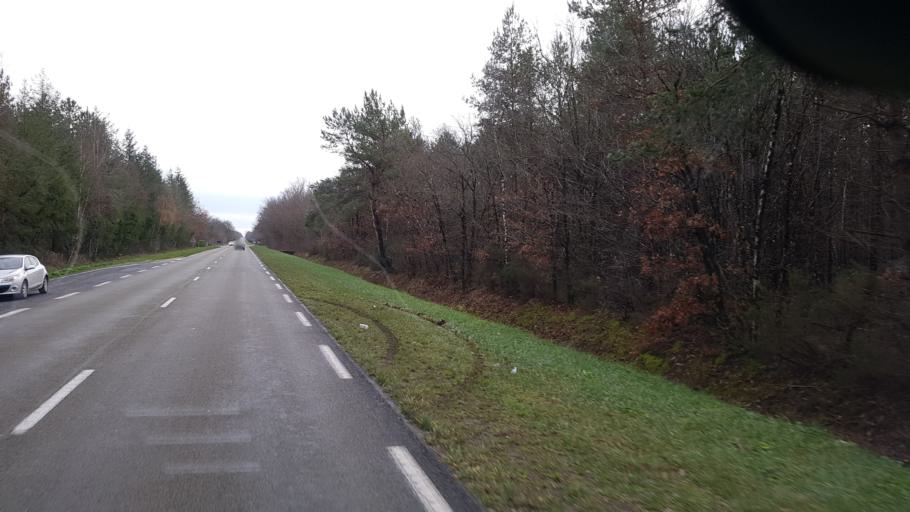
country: FR
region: Centre
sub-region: Departement du Loiret
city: Menestreau-en-Villette
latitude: 47.6668
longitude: 1.9760
